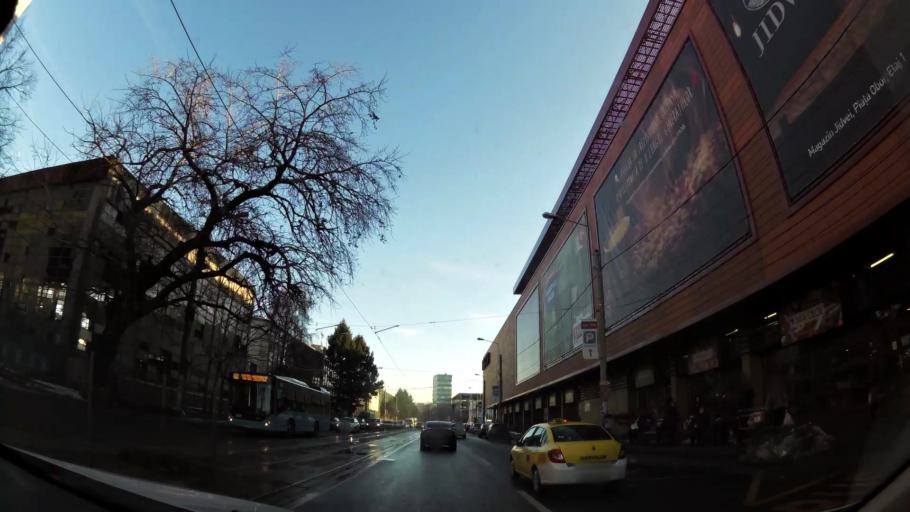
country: RO
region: Bucuresti
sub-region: Municipiul Bucuresti
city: Bucharest
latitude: 44.4503
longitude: 26.1301
